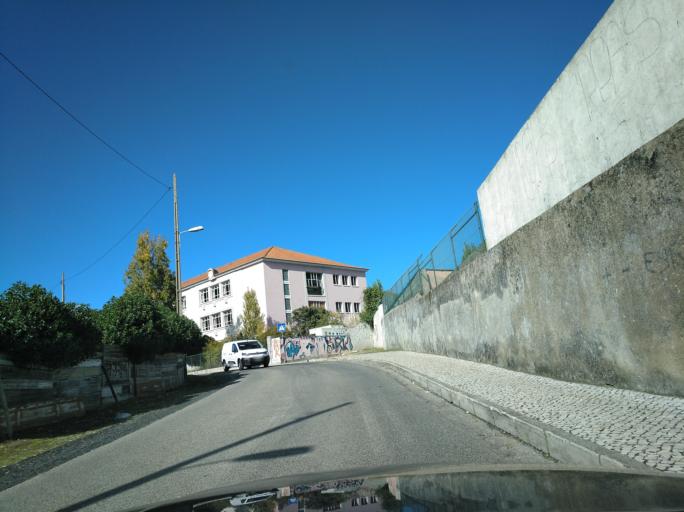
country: PT
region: Lisbon
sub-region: Lisbon
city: Lisbon
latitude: 38.7351
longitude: -9.1092
